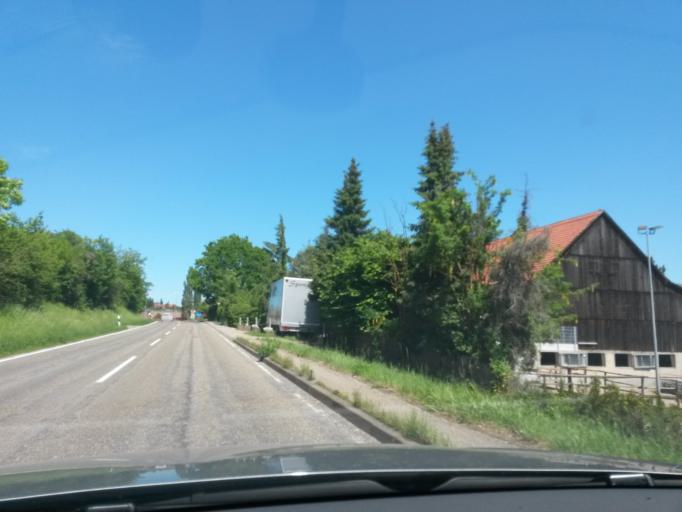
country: DE
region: Baden-Wuerttemberg
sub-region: Regierungsbezirk Stuttgart
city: Weil der Stadt
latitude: 48.7458
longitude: 8.8709
